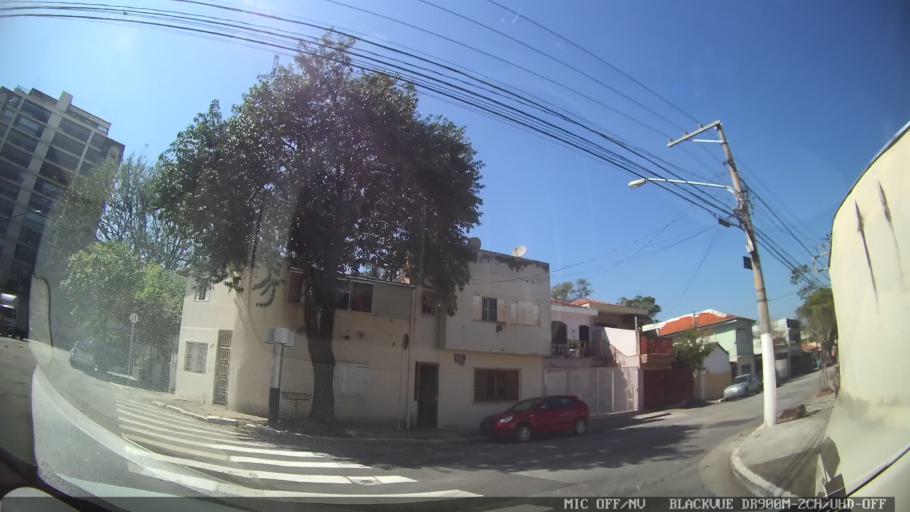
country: BR
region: Sao Paulo
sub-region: Sao Paulo
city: Sao Paulo
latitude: -23.5102
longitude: -46.6510
